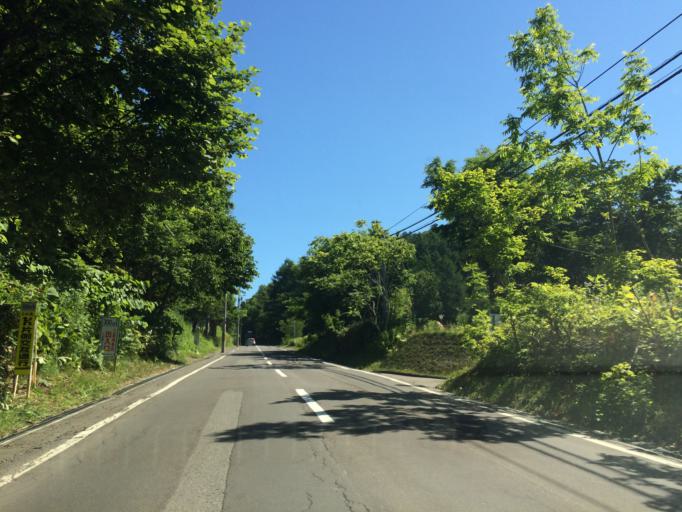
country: JP
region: Hokkaido
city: Sapporo
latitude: 43.0350
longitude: 141.2834
